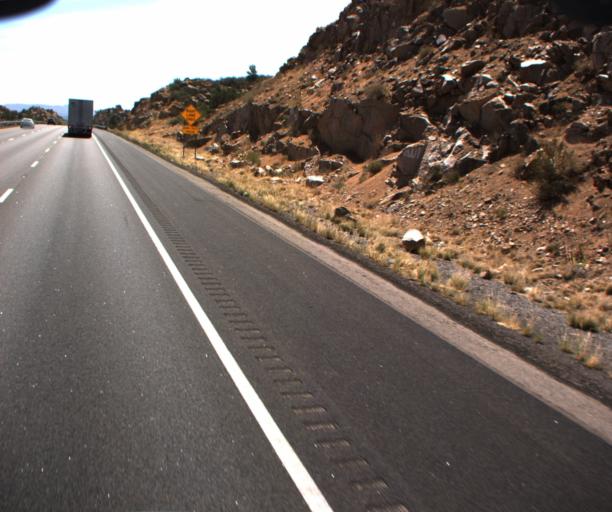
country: US
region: Arizona
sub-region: Mohave County
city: Peach Springs
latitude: 35.1854
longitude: -113.4053
